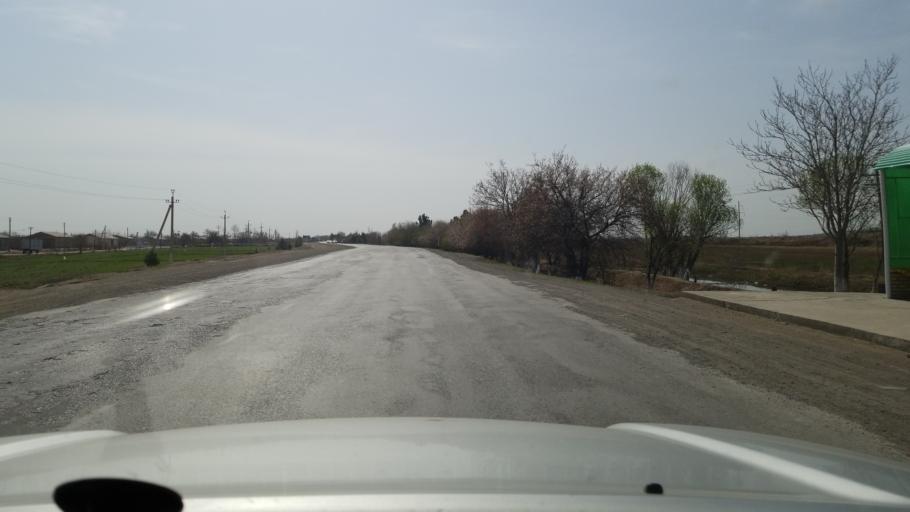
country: TM
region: Lebap
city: Sayat
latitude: 38.8280
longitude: 63.8240
